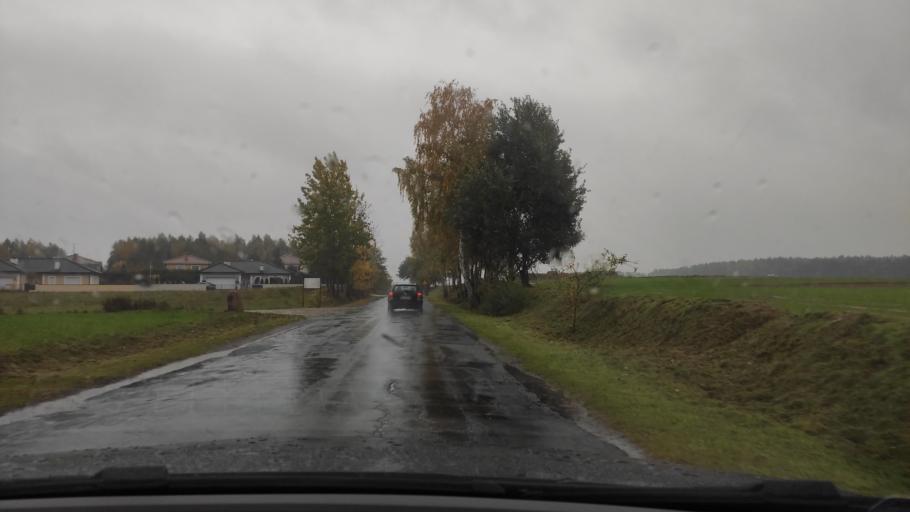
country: PL
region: Greater Poland Voivodeship
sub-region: Powiat poznanski
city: Kornik
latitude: 52.2086
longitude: 17.1015
